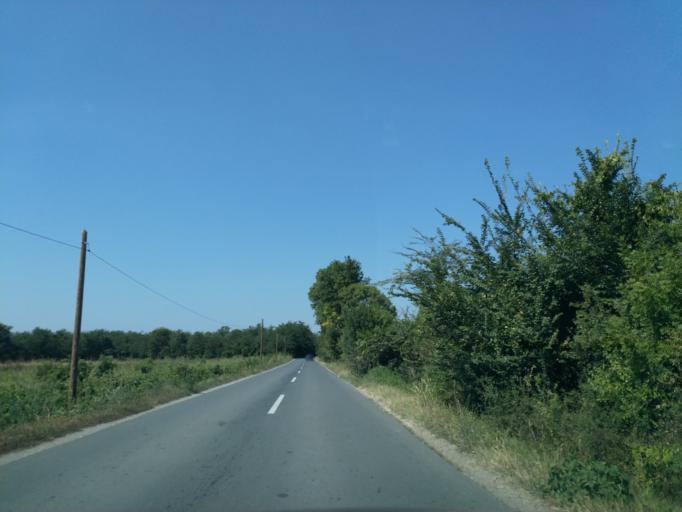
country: RS
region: Central Serbia
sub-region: Rasinski Okrug
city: Trstenik
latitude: 43.6243
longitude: 21.1600
